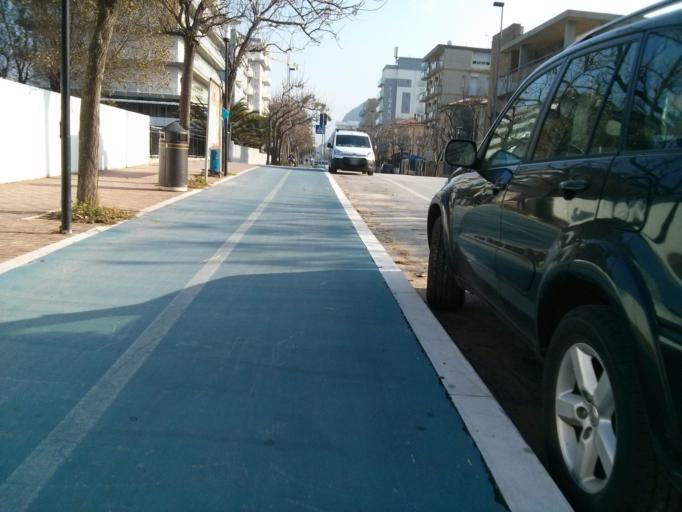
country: IT
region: The Marches
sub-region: Provincia di Pesaro e Urbino
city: Pesaro
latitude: 43.9097
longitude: 12.9237
